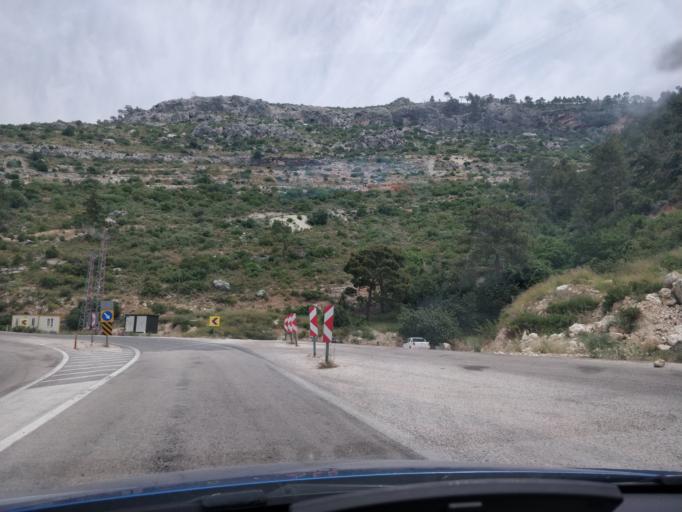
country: TR
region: Mersin
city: Tasucu
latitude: 36.3919
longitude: 33.8392
